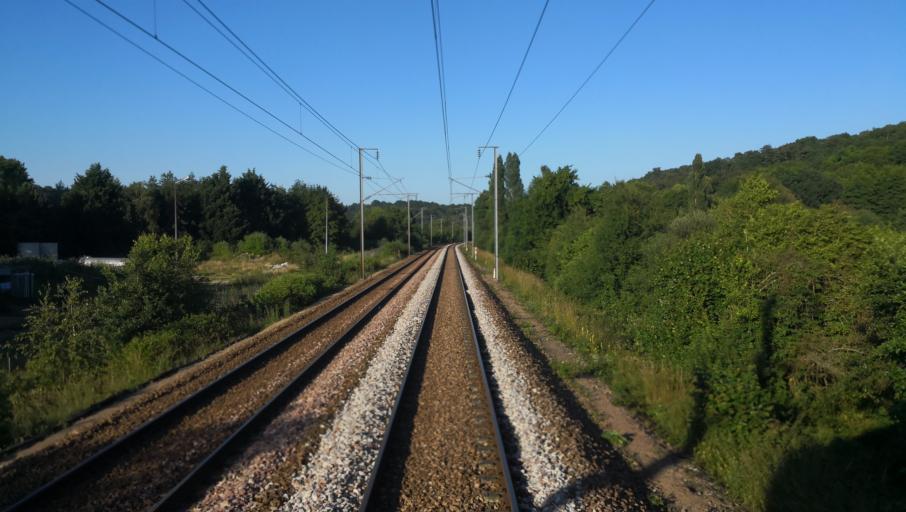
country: FR
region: Haute-Normandie
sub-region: Departement de l'Eure
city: Menneval
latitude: 49.0940
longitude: 0.6214
